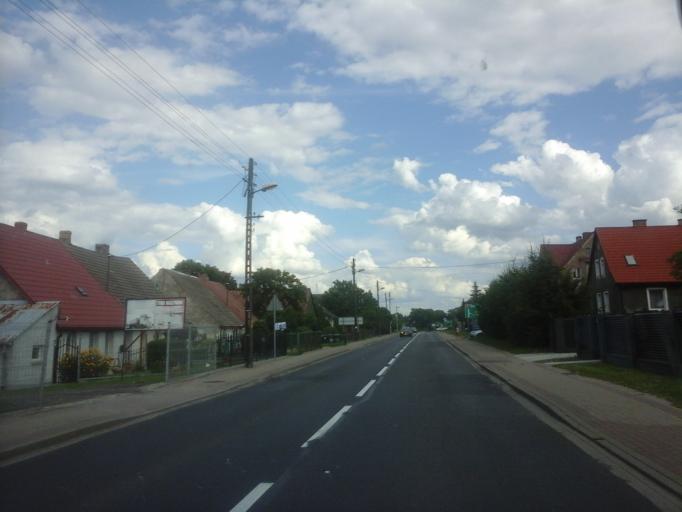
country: PL
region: West Pomeranian Voivodeship
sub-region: Powiat stargardzki
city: Suchan
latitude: 53.2794
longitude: 15.3271
